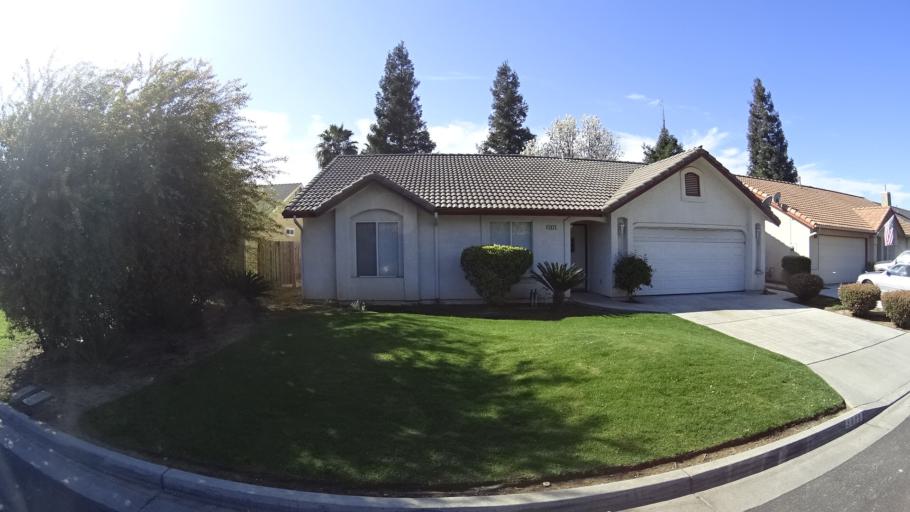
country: US
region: California
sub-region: Fresno County
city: West Park
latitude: 36.7961
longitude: -119.8922
